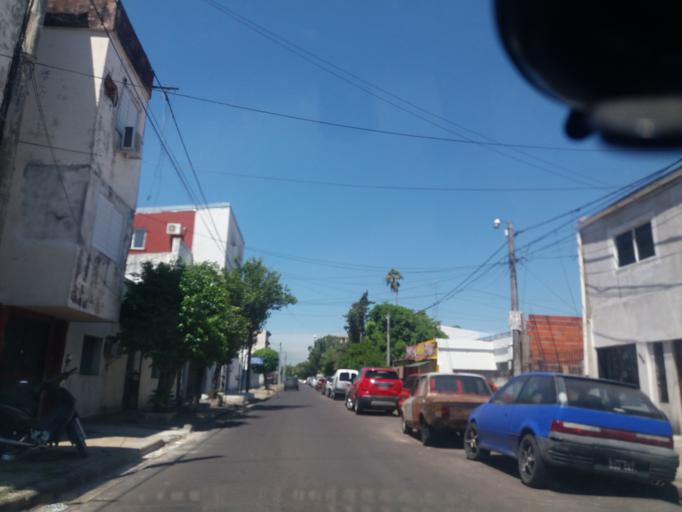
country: AR
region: Corrientes
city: Corrientes
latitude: -27.4797
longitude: -58.8450
